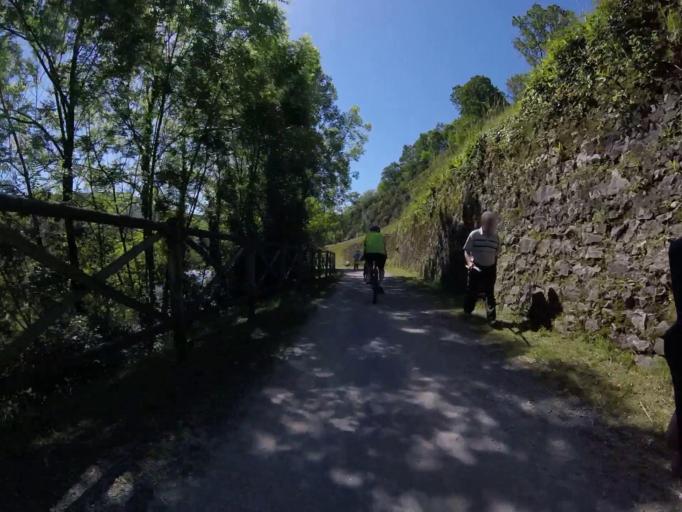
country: ES
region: Basque Country
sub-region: Provincia de Guipuzcoa
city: Irun
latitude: 43.3331
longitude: -1.7528
